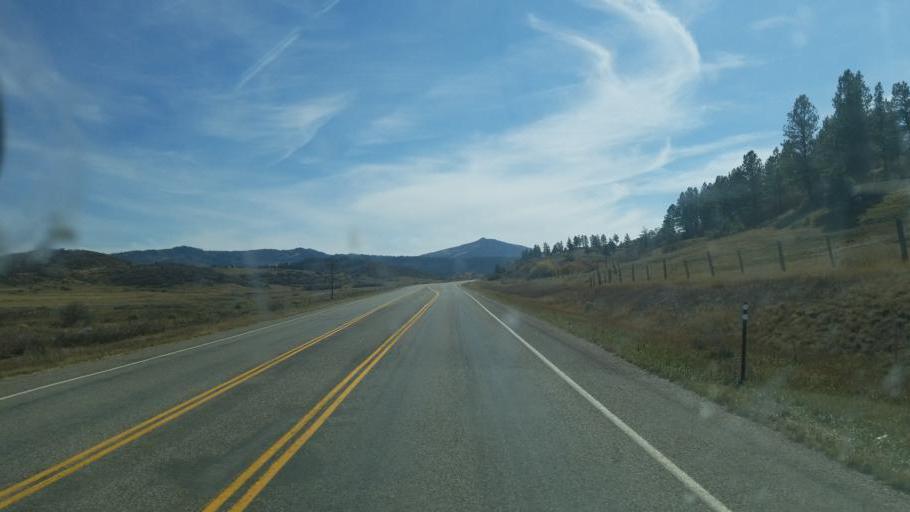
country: US
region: New Mexico
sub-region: Rio Arriba County
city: Dulce
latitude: 37.0160
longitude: -106.8087
